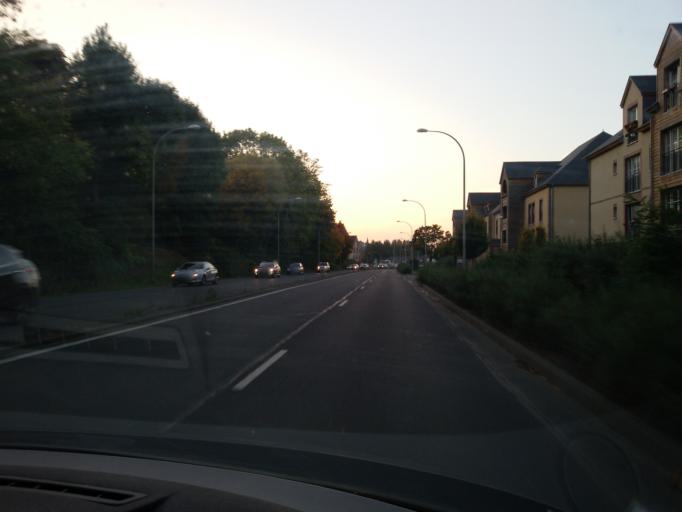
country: FR
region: Lower Normandy
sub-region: Departement du Calvados
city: Honfleur
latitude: 49.4164
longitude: 0.2428
